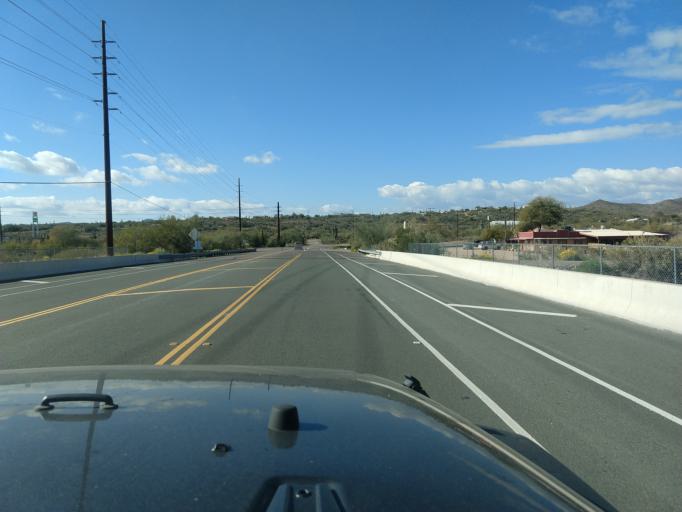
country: US
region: Arizona
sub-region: Maricopa County
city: New River
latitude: 33.9184
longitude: -112.1389
